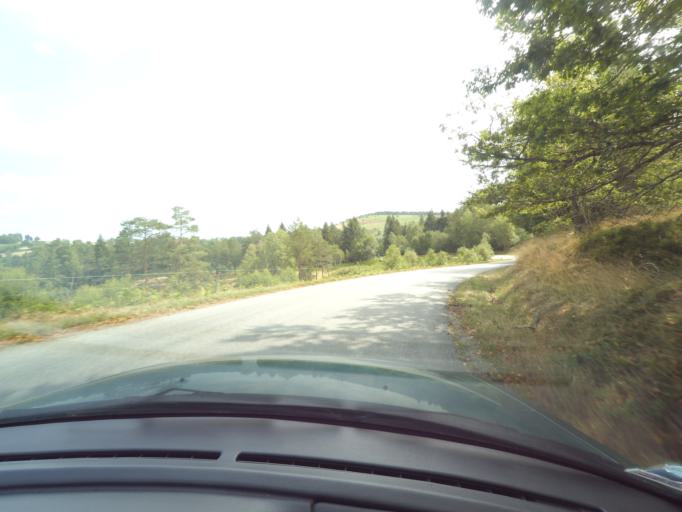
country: FR
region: Limousin
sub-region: Departement de la Correze
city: Bugeat
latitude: 45.7336
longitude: 1.9926
